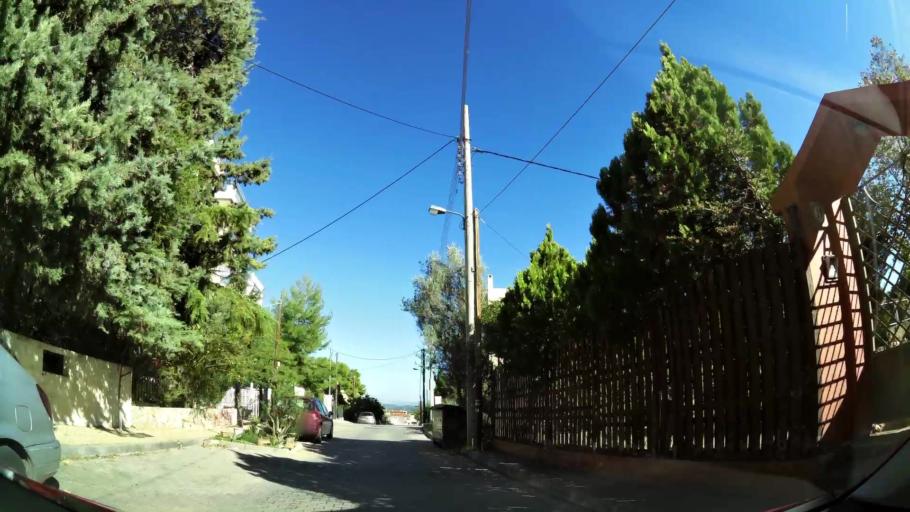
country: GR
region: Attica
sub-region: Nomarchia Anatolikis Attikis
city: Leondarion
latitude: 37.9881
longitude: 23.8468
